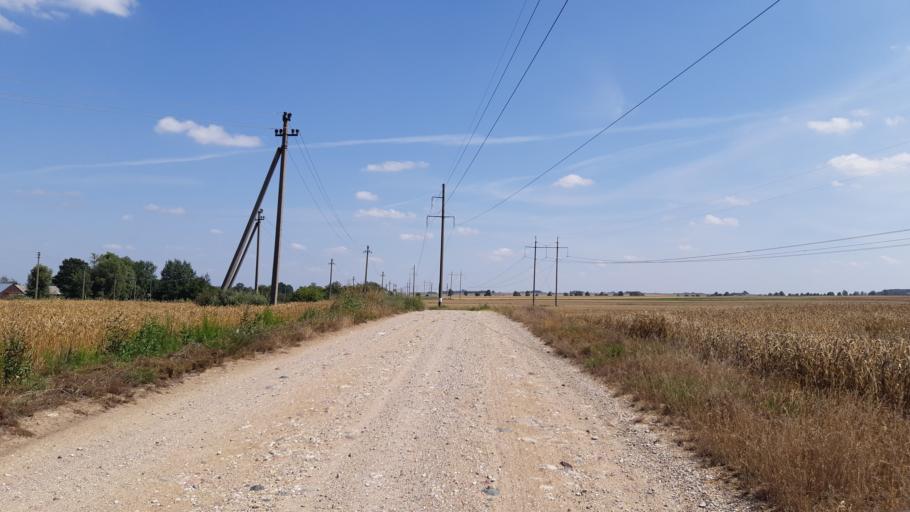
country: LT
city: Virbalis
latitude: 54.6188
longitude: 22.8109
